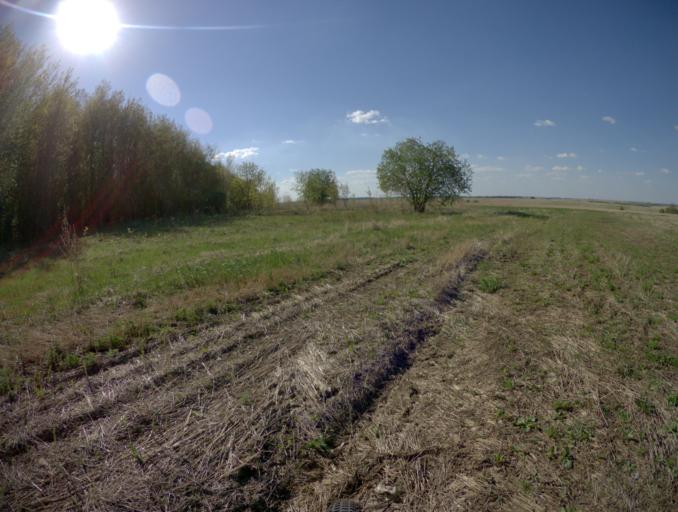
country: RU
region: Vladimir
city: Suzdal'
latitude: 56.3214
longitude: 40.2280
